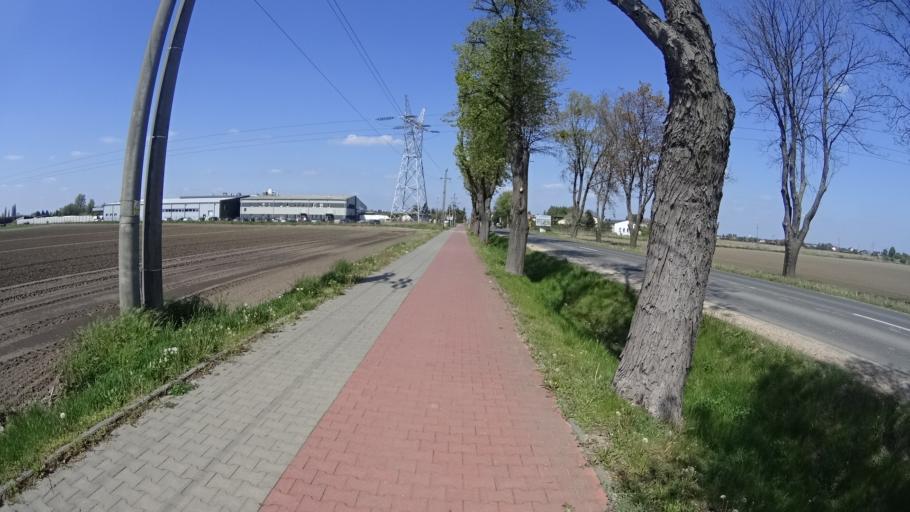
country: PL
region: Masovian Voivodeship
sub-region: Powiat warszawski zachodni
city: Stare Babice
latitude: 52.2382
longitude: 20.8171
